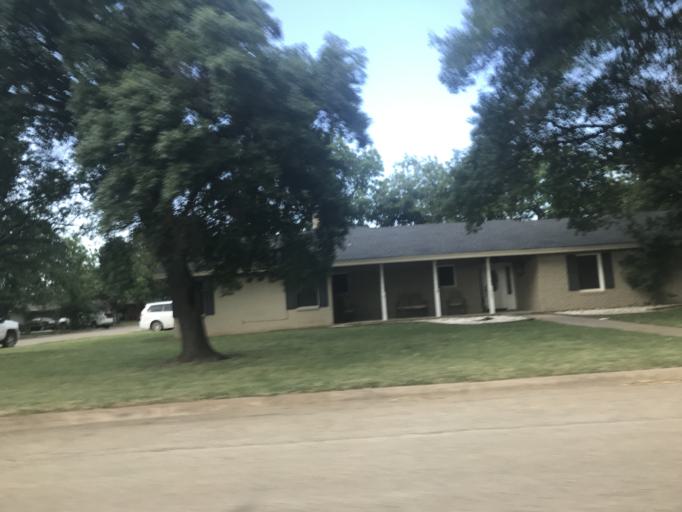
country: US
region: Texas
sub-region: Taylor County
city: Abilene
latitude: 32.4257
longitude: -99.7667
